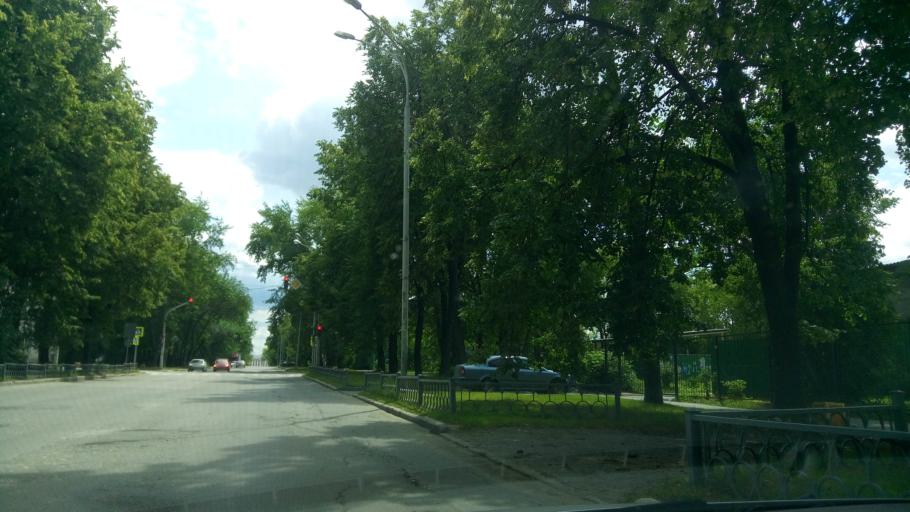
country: RU
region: Sverdlovsk
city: Yekaterinburg
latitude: 56.8865
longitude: 60.6246
